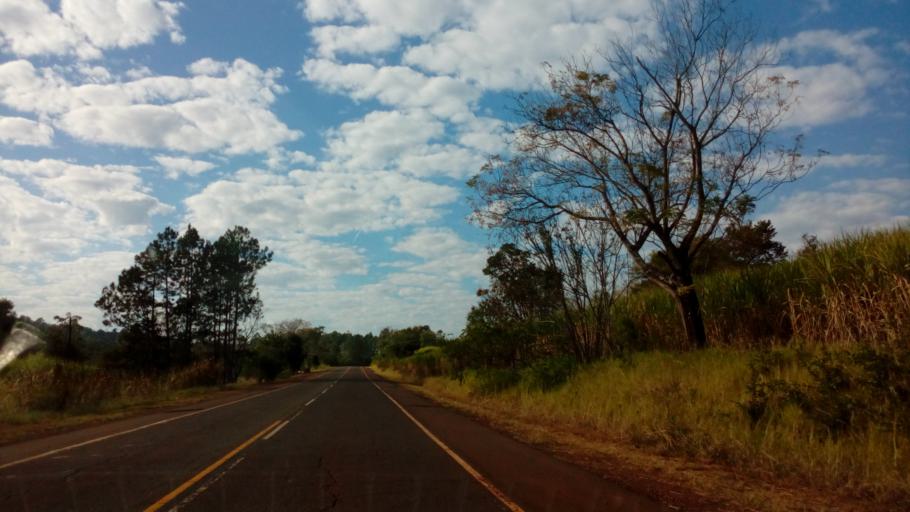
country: AR
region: Misiones
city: Ruiz de Montoya
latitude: -27.0598
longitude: -55.0021
